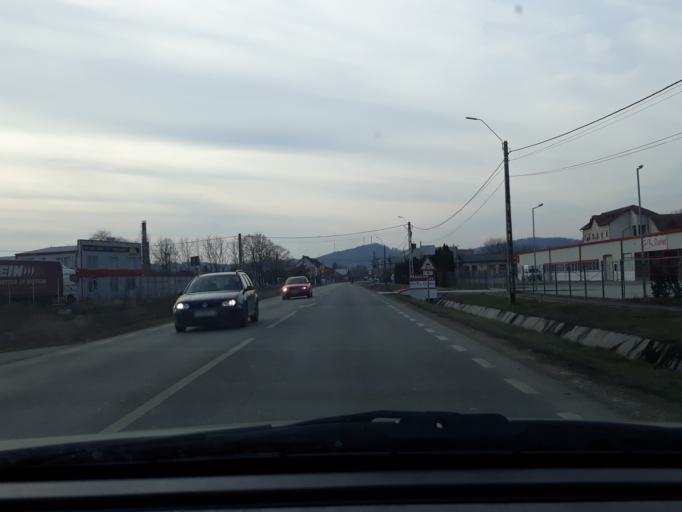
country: RO
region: Salaj
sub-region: Oras Simleu Silvaniei
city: Simleu Silvaniei
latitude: 47.2301
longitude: 22.8180
